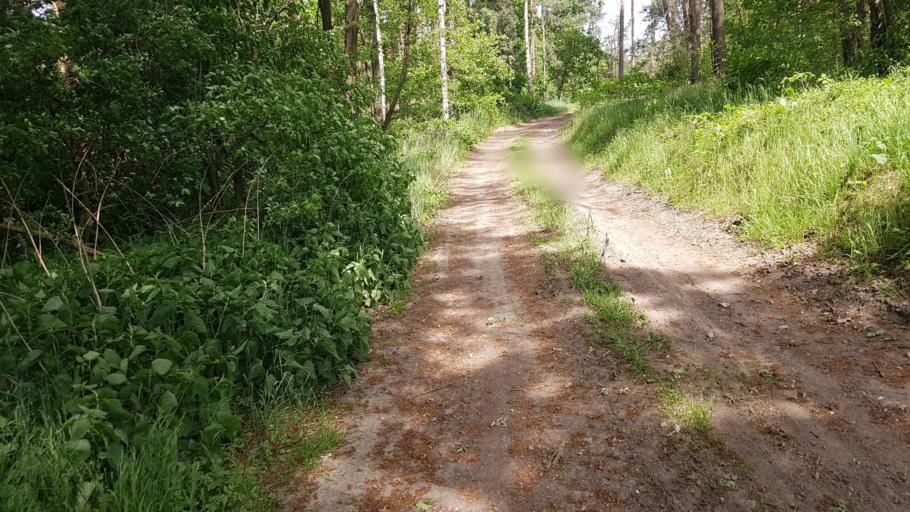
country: DE
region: Brandenburg
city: Grosskmehlen
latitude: 51.3735
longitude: 13.7046
